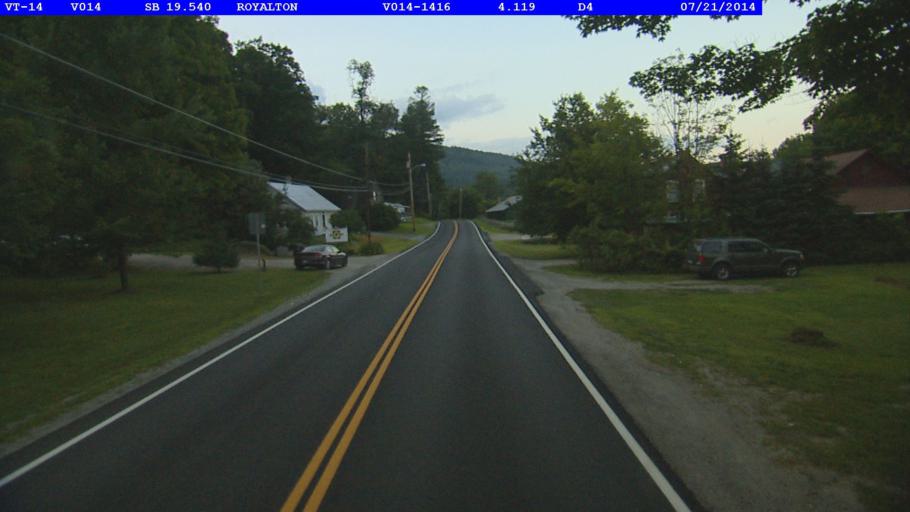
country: US
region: Vermont
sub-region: Orange County
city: Randolph
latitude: 43.8176
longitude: -72.5449
